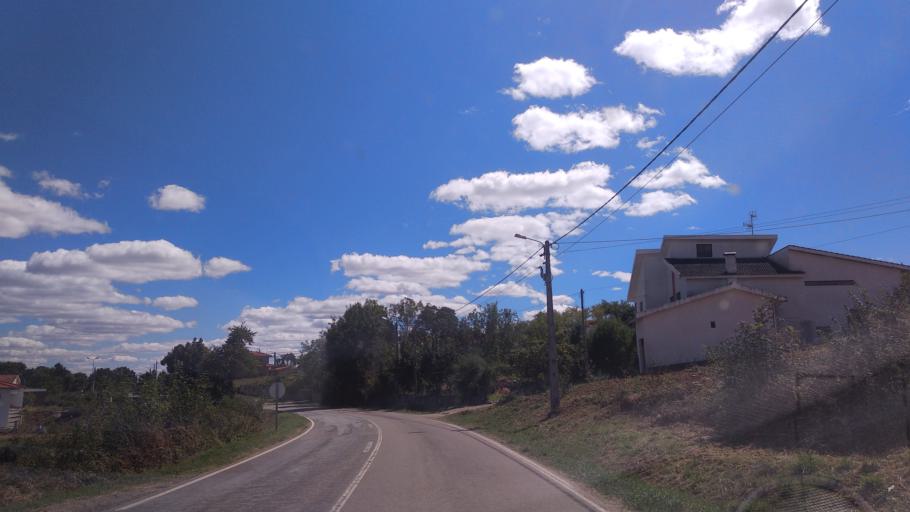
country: PT
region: Braganca
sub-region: Braganca Municipality
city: Braganca
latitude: 41.7748
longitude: -6.7622
